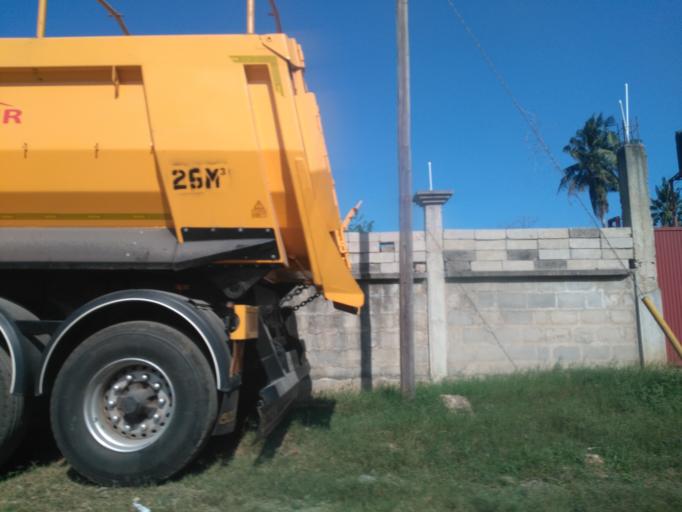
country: TZ
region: Dar es Salaam
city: Magomeni
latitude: -6.7798
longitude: 39.2680
